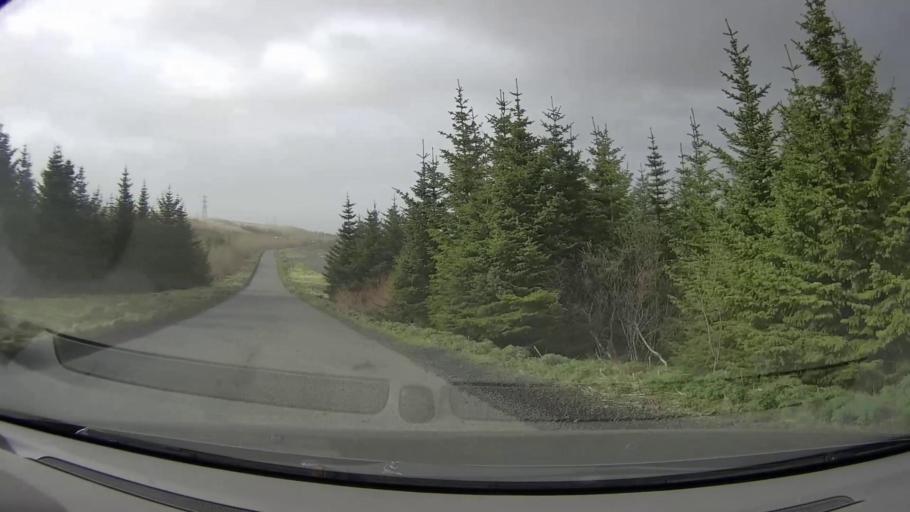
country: IS
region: Capital Region
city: Hafnarfjoerdur
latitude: 64.0435
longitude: -21.9171
